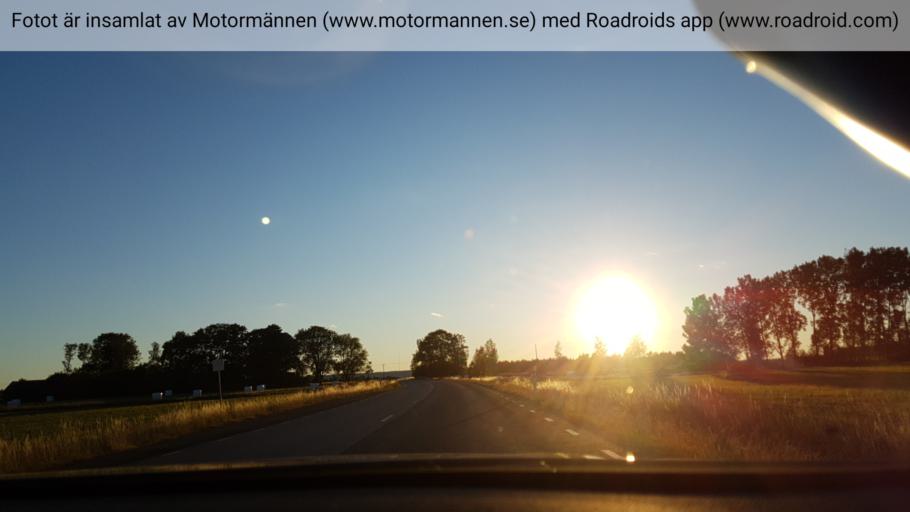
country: SE
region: Vaestra Goetaland
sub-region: Tidaholms Kommun
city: Olofstorp
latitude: 58.3710
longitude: 14.0048
